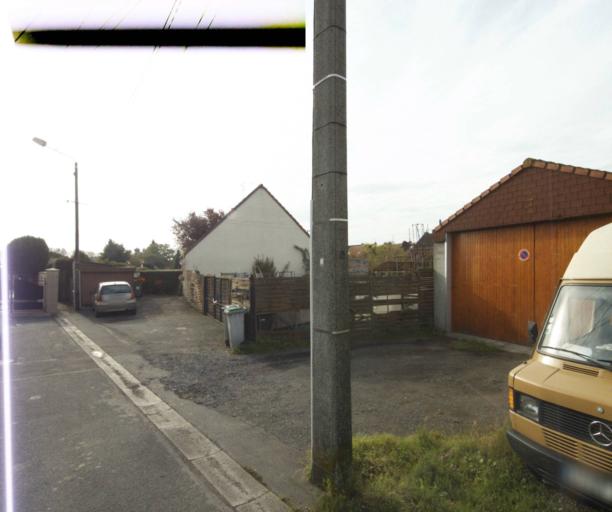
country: FR
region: Nord-Pas-de-Calais
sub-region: Departement du Nord
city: Don
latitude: 50.5566
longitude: 2.9121
